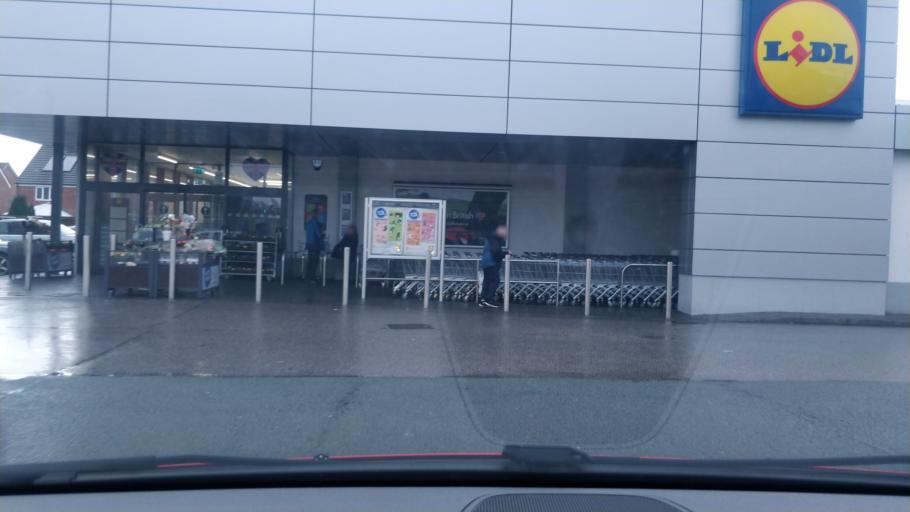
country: GB
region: England
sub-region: Knowsley
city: Huyton
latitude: 53.4219
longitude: -2.8627
